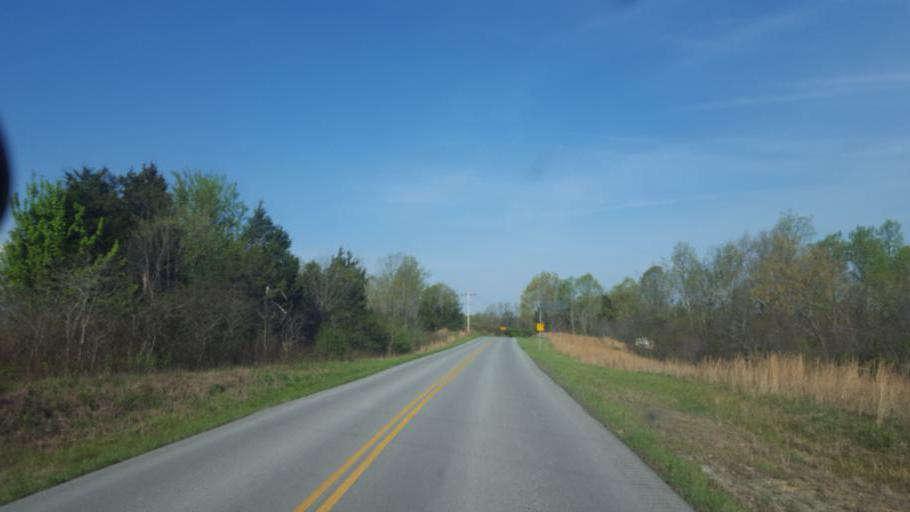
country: US
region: Kentucky
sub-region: Hart County
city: Munfordville
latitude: 37.3150
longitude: -86.0779
